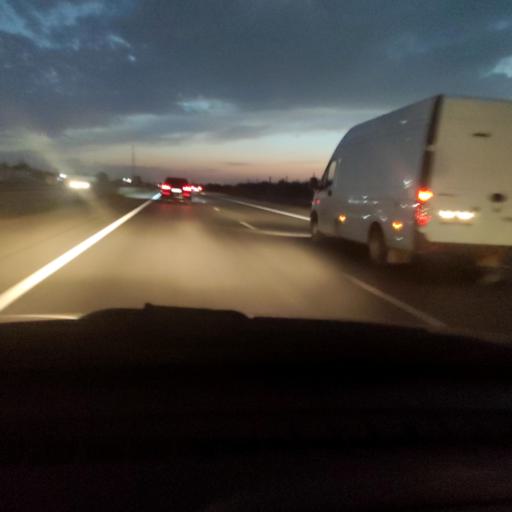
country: RU
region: Samara
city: Tol'yatti
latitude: 53.5707
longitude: 49.3833
